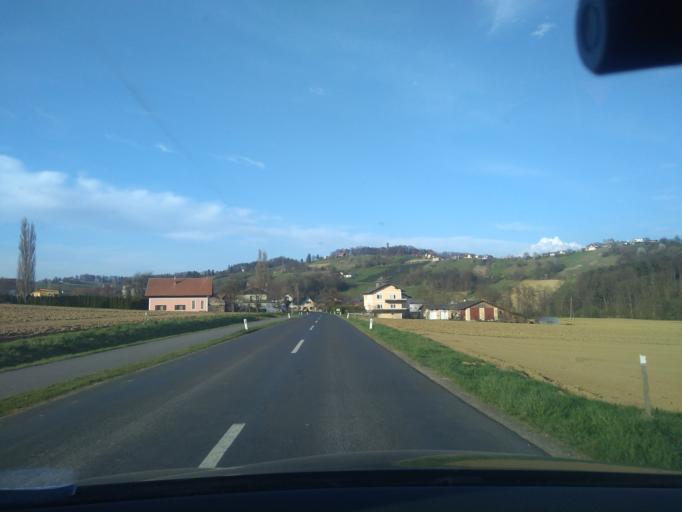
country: AT
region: Styria
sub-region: Politischer Bezirk Suedoststeiermark
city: Sankt Peter am Ottersbach
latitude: 46.8086
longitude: 15.7598
